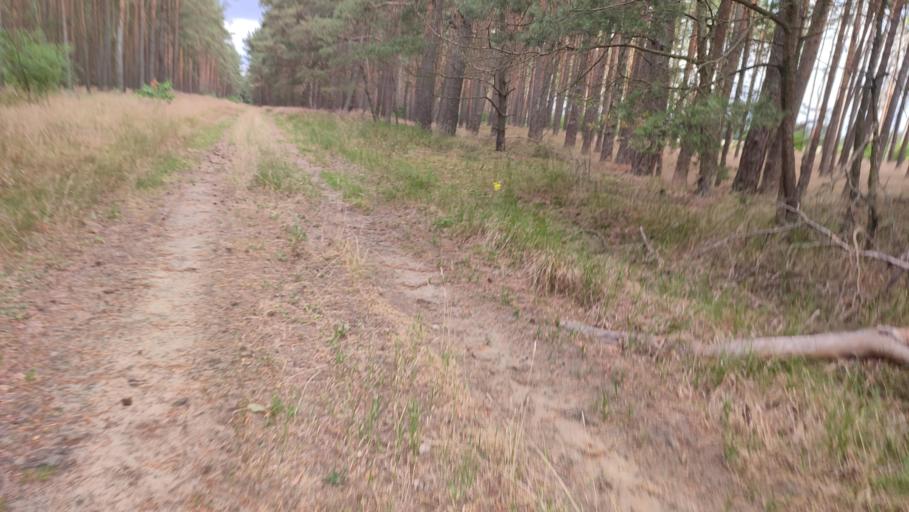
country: DE
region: Lower Saxony
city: Hitzacker
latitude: 53.1975
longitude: 11.0925
